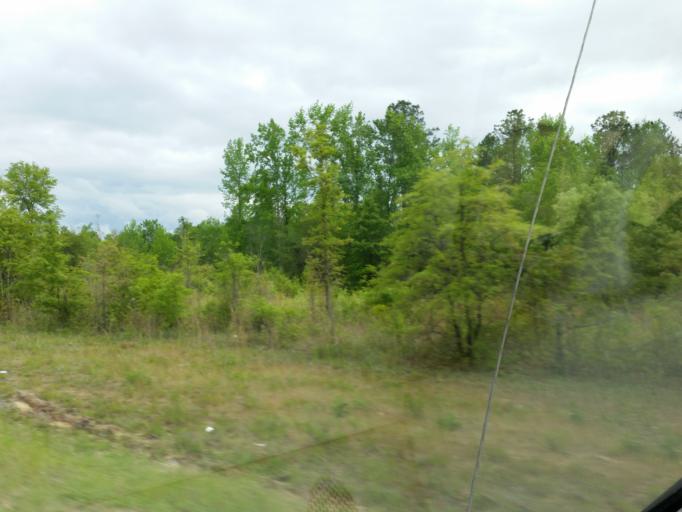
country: US
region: Georgia
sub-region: Crawford County
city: Knoxville
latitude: 32.7227
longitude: -83.9830
